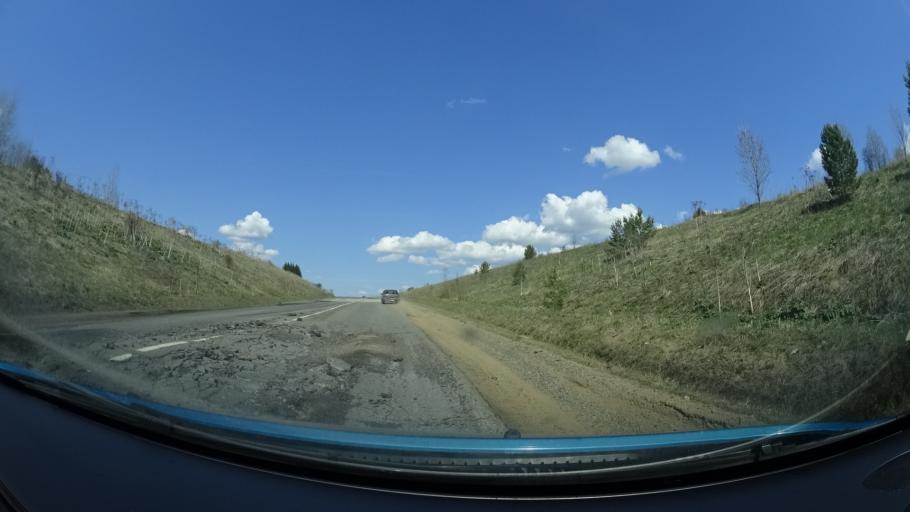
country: RU
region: Perm
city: Osa
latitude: 57.2606
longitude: 55.5756
